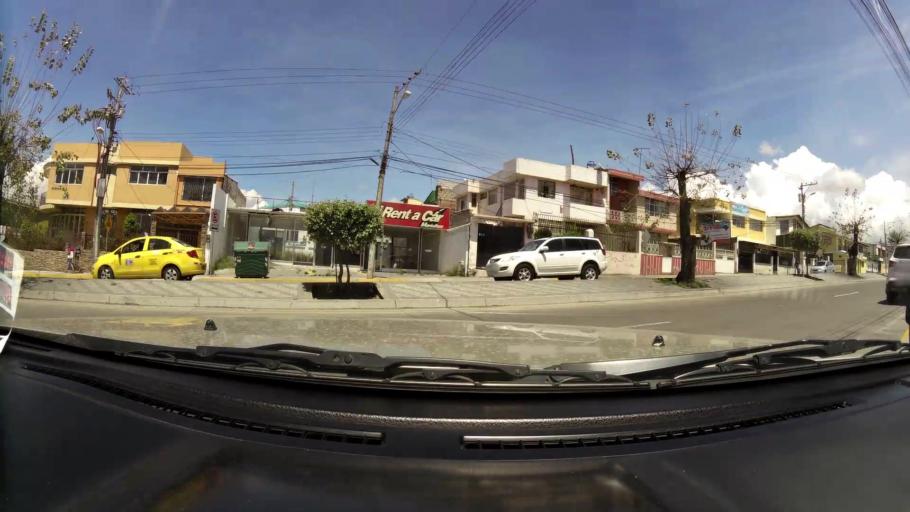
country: EC
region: Chimborazo
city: Riobamba
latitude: -1.6596
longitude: -78.6616
